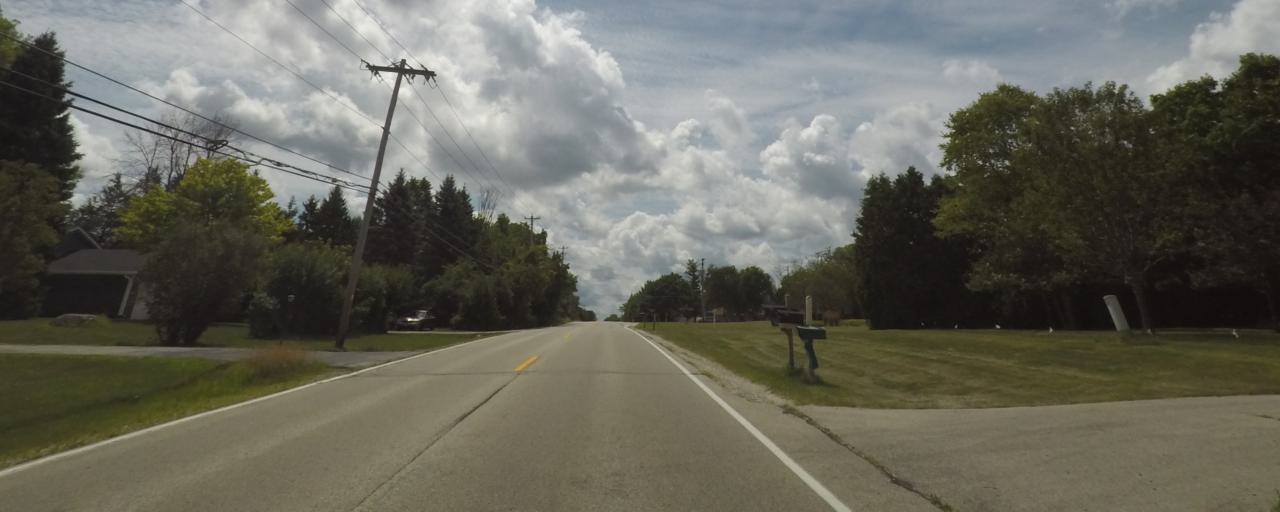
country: US
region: Wisconsin
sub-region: Milwaukee County
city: Hales Corners
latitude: 42.9680
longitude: -88.0690
